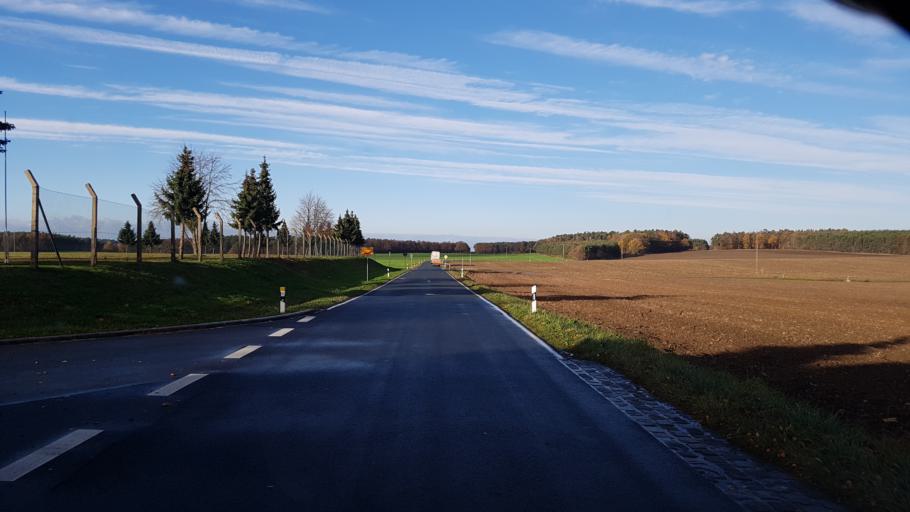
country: DE
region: Brandenburg
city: Ortrand
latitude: 51.3448
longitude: 13.7692
